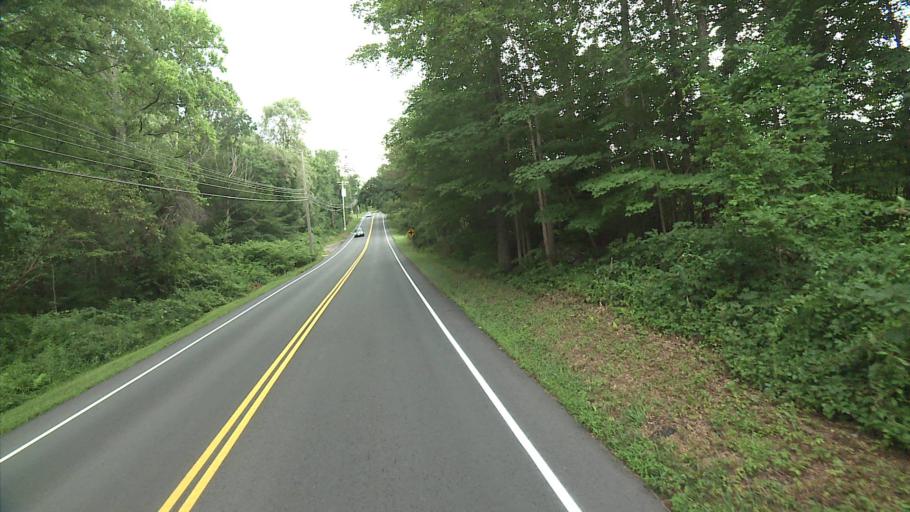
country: US
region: Connecticut
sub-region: New Haven County
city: Heritage Village
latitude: 41.5470
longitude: -73.2929
